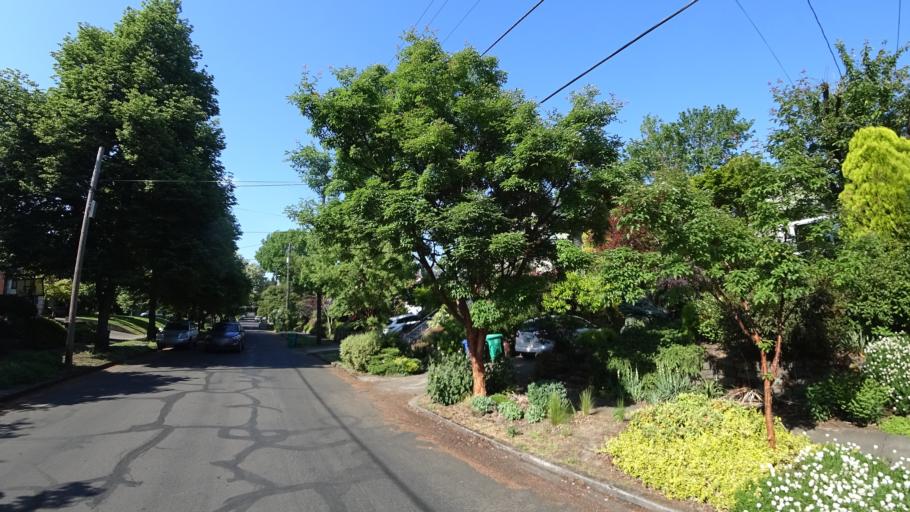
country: US
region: Oregon
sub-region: Multnomah County
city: Portland
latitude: 45.5496
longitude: -122.6464
